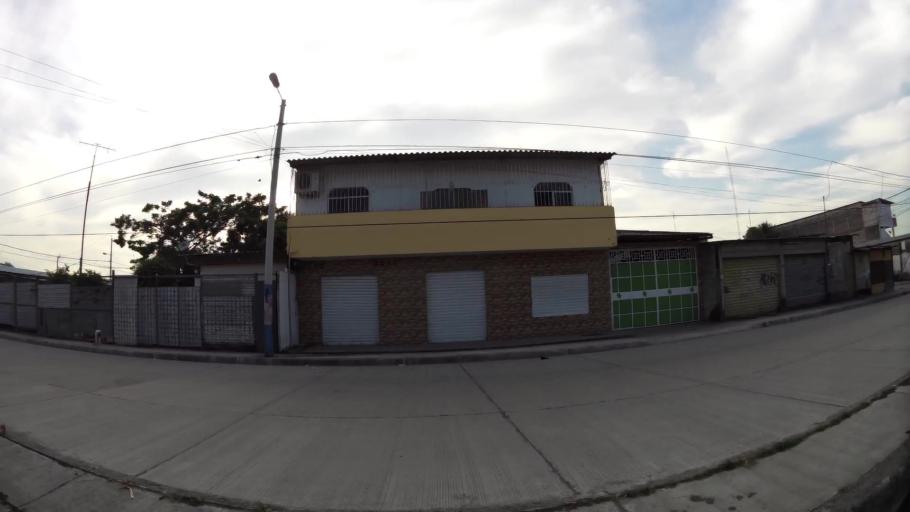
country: EC
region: Guayas
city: Eloy Alfaro
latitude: -2.0939
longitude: -79.9032
